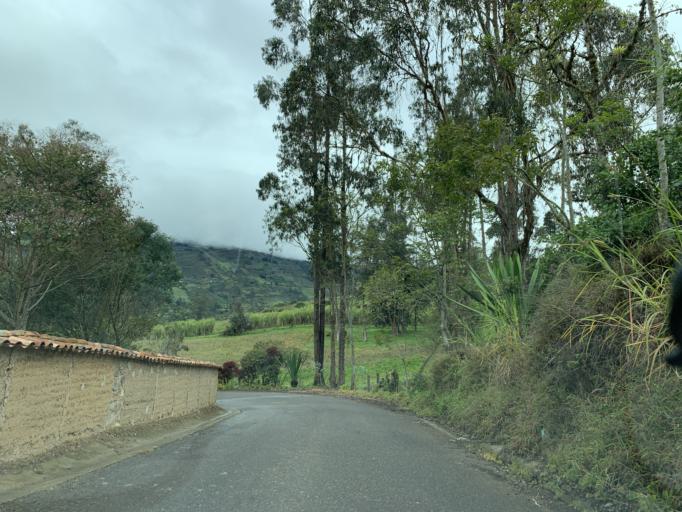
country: CO
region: Boyaca
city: Tibana
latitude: 5.3114
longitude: -73.4180
